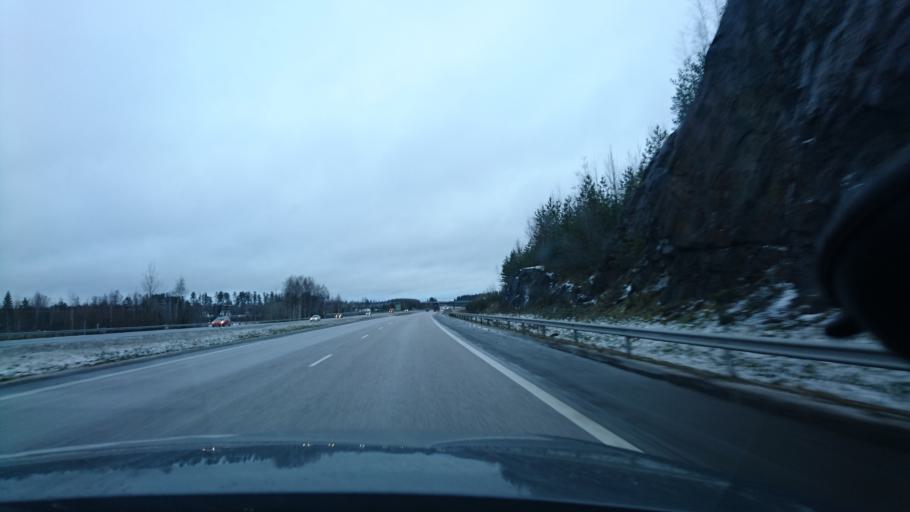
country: FI
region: Uusimaa
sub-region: Helsinki
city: Maentsaelae
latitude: 60.6391
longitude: 25.2988
